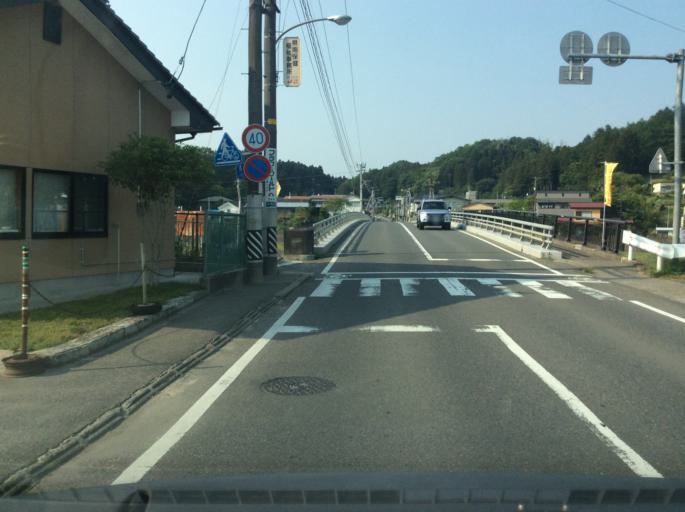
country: JP
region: Fukushima
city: Sukagawa
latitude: 37.1322
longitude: 140.2220
